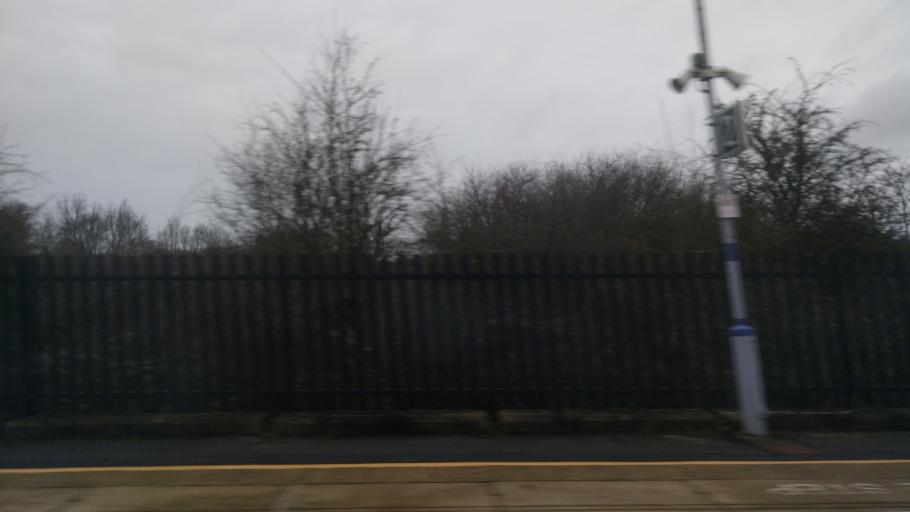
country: GB
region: England
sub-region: Kent
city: Staplehurst
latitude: 51.1717
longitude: 0.5493
